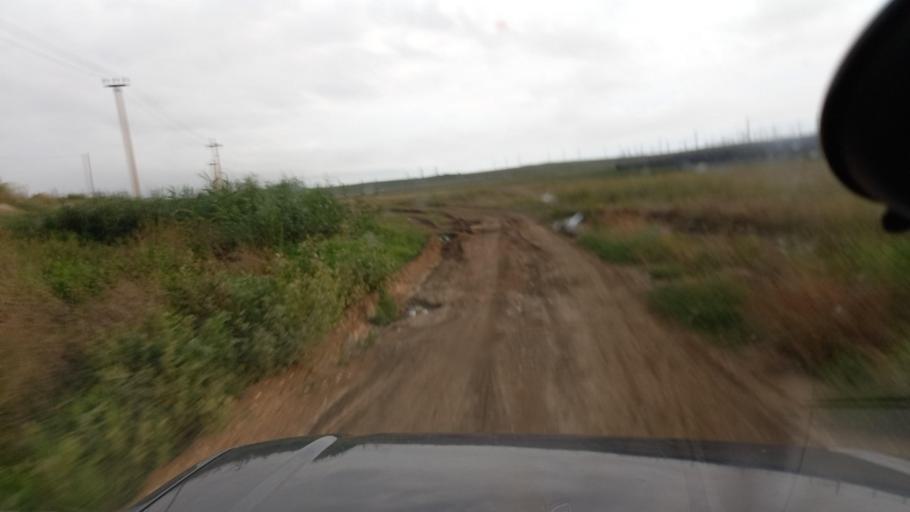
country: RU
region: Krasnodarskiy
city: Taman'
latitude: 45.2103
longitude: 36.7587
